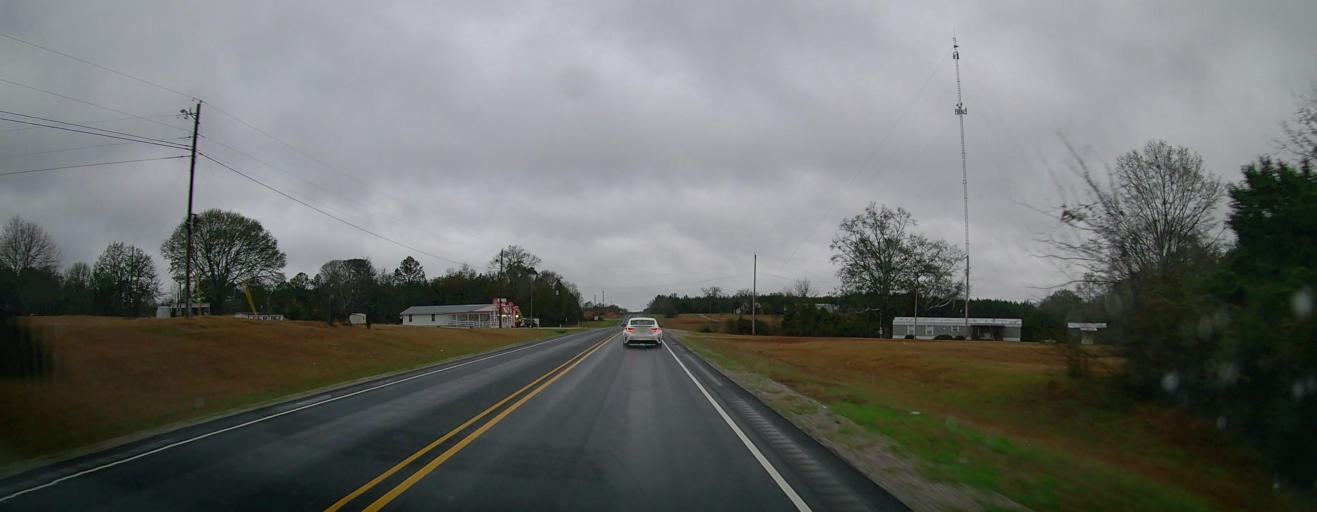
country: US
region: Alabama
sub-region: Chilton County
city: Clanton
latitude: 32.6522
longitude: -86.7664
